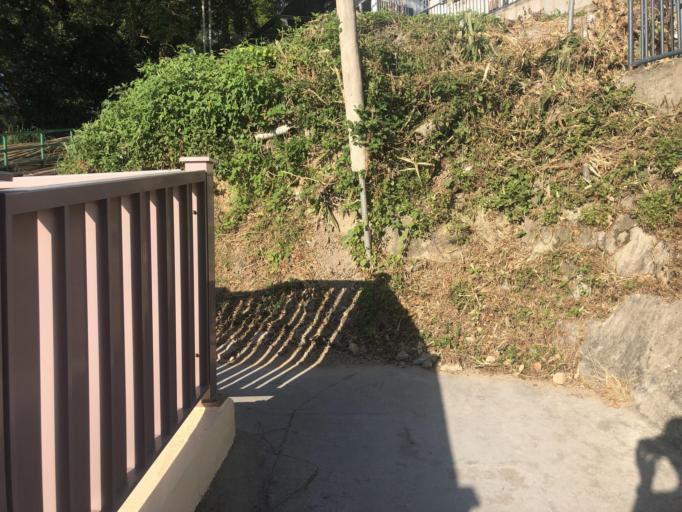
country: HK
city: Yung Shue Wan
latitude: 22.2141
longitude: 114.0265
